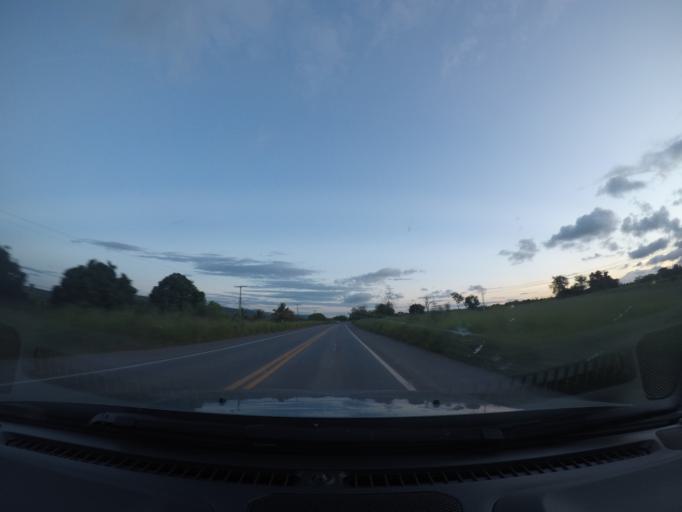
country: BR
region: Bahia
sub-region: Seabra
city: Seabra
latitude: -12.4430
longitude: -41.7528
